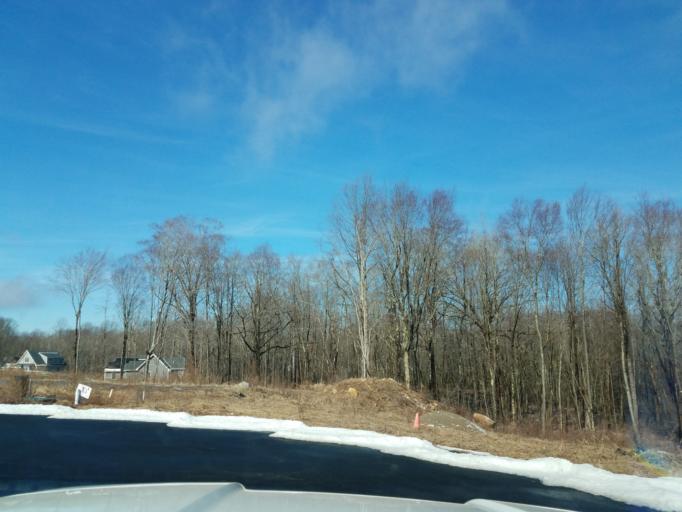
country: US
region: Connecticut
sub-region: New London County
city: Ledyard Center
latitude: 41.4480
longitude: -72.0133
